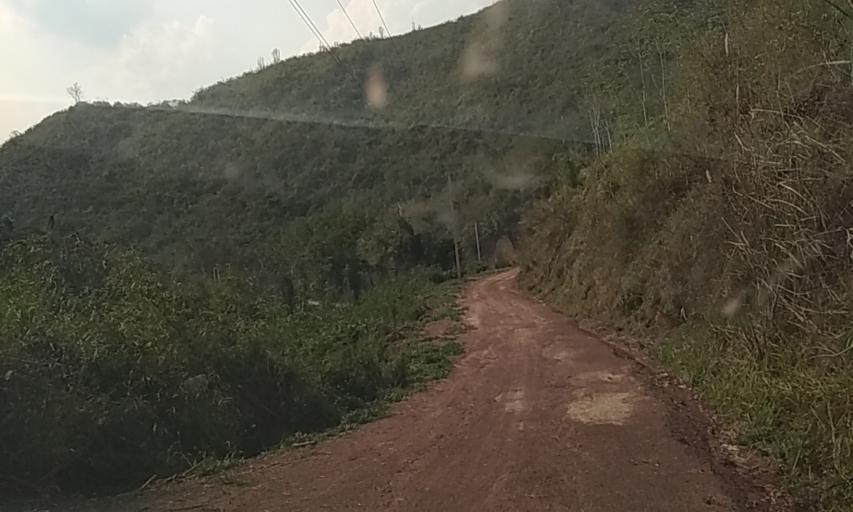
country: LA
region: Louangphabang
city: Louangphabang
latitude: 20.0455
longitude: 101.8414
